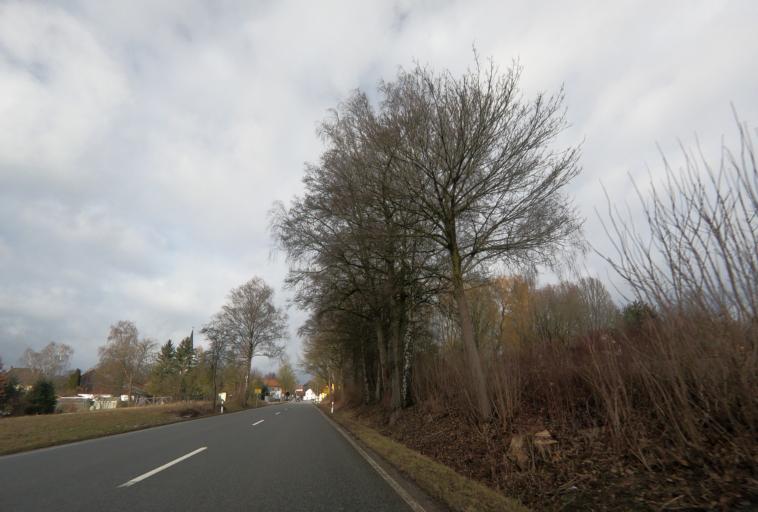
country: DE
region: Bavaria
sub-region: Lower Bavaria
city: Mallersdorf-Pfaffenberg
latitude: 48.7826
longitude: 12.1838
